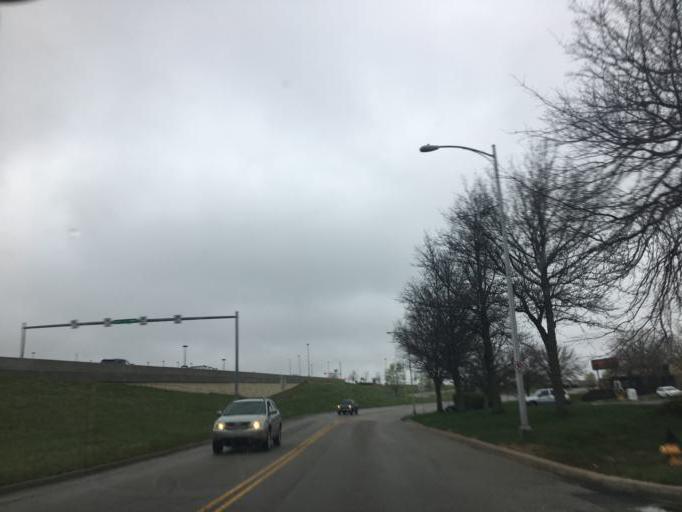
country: US
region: Kansas
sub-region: Johnson County
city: Lenexa
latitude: 38.9732
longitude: -94.7178
